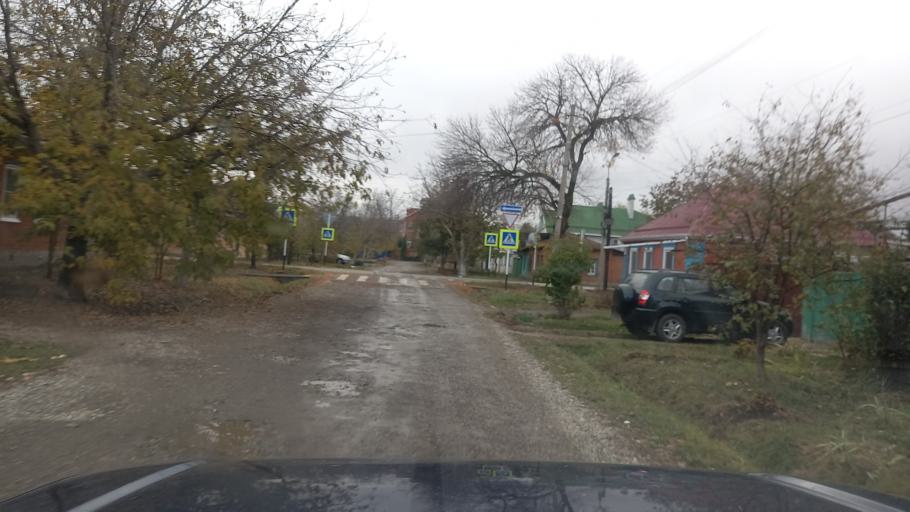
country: RU
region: Adygeya
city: Maykop
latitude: 44.6027
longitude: 40.0857
